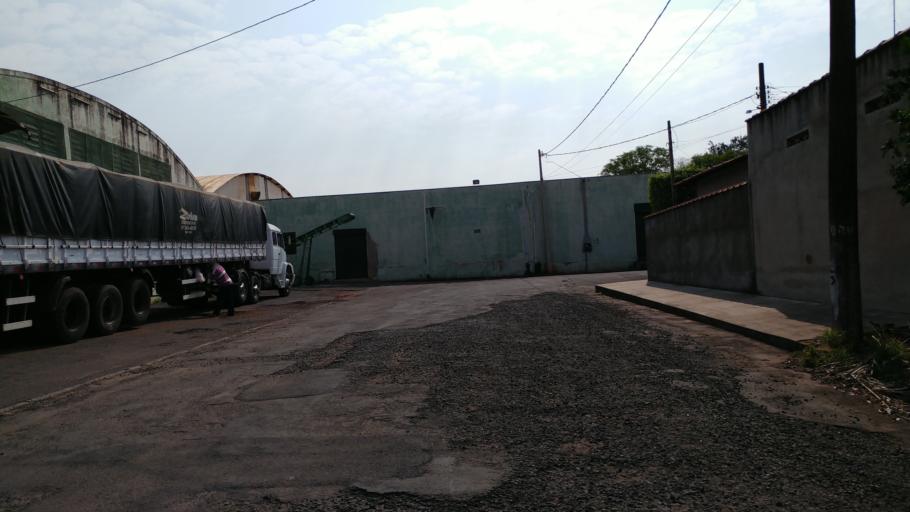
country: BR
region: Sao Paulo
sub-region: Paraguacu Paulista
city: Paraguacu Paulista
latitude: -22.4167
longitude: -50.5725
